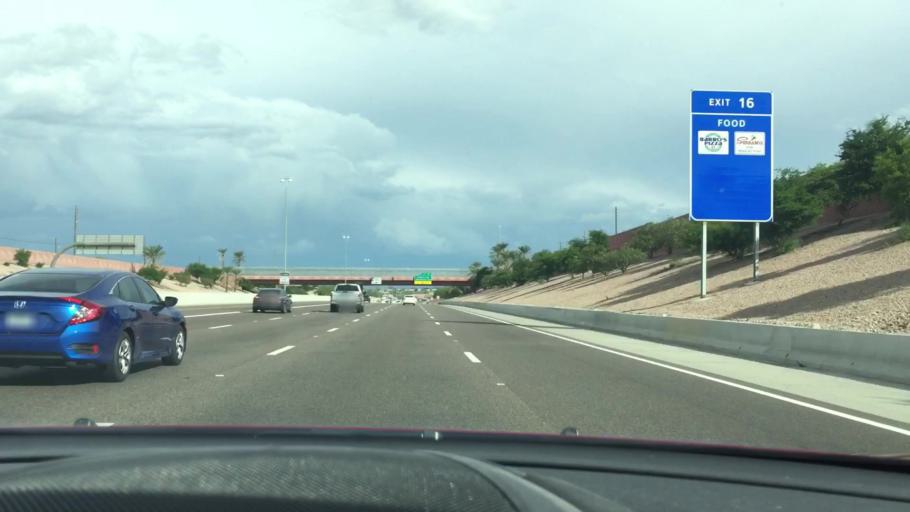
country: US
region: Arizona
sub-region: Maricopa County
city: Mesa
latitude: 33.4650
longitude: -111.8071
